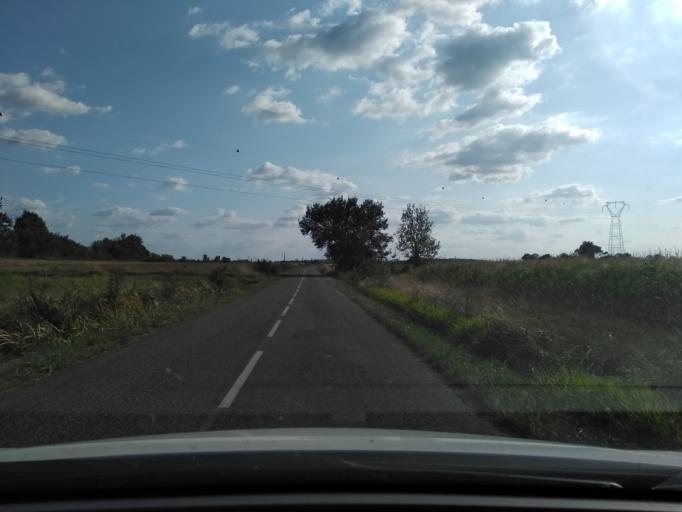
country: FR
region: Midi-Pyrenees
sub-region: Departement du Tarn-et-Garonne
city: Montech
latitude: 43.9811
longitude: 1.2510
